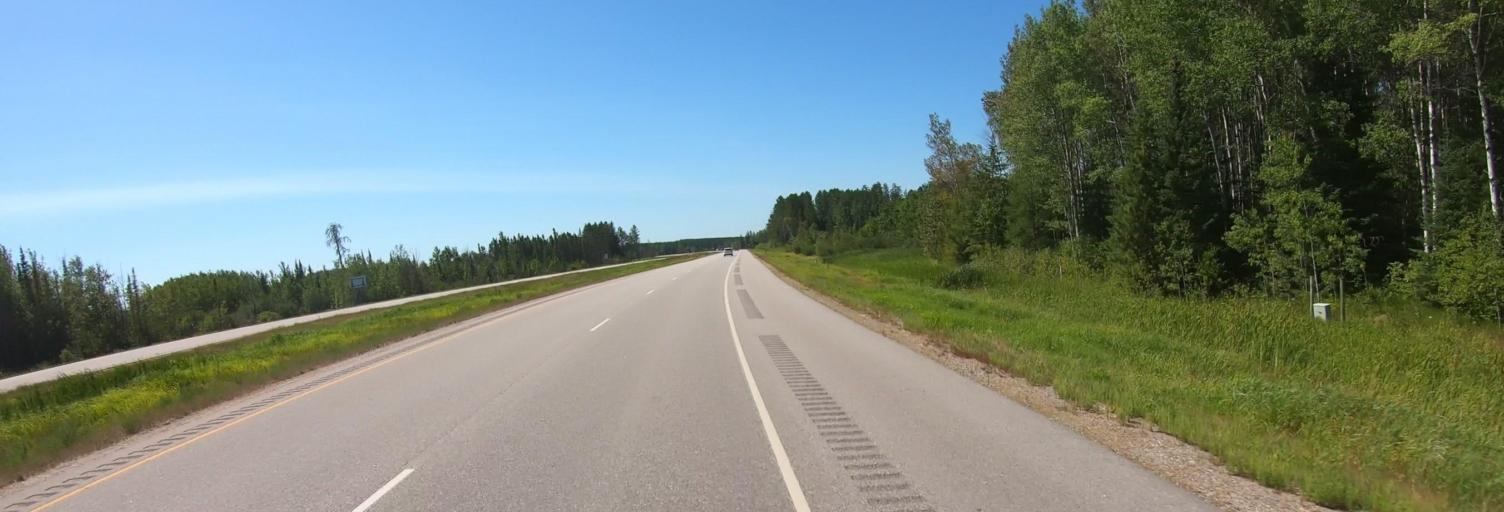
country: US
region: Minnesota
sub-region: Saint Louis County
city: Mountain Iron
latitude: 47.7424
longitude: -92.6479
